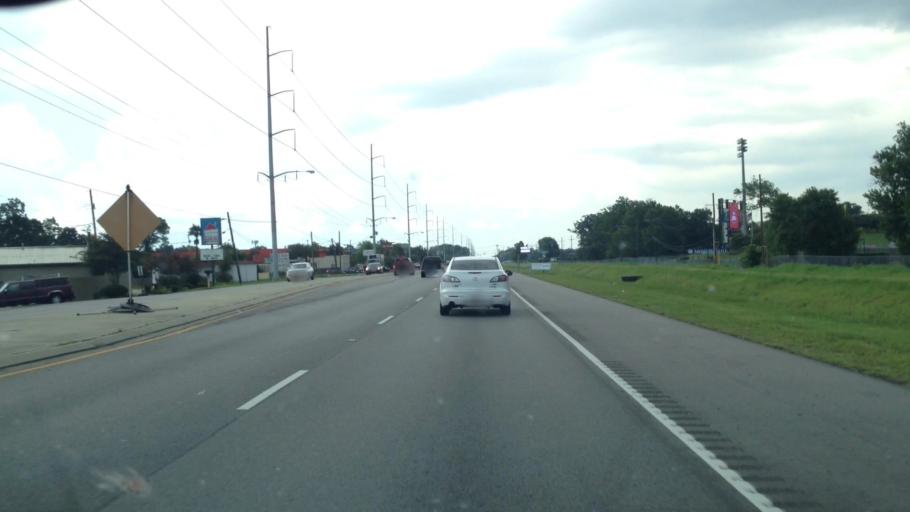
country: US
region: Louisiana
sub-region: Jefferson Parish
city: River Ridge
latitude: 29.9771
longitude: -90.2020
